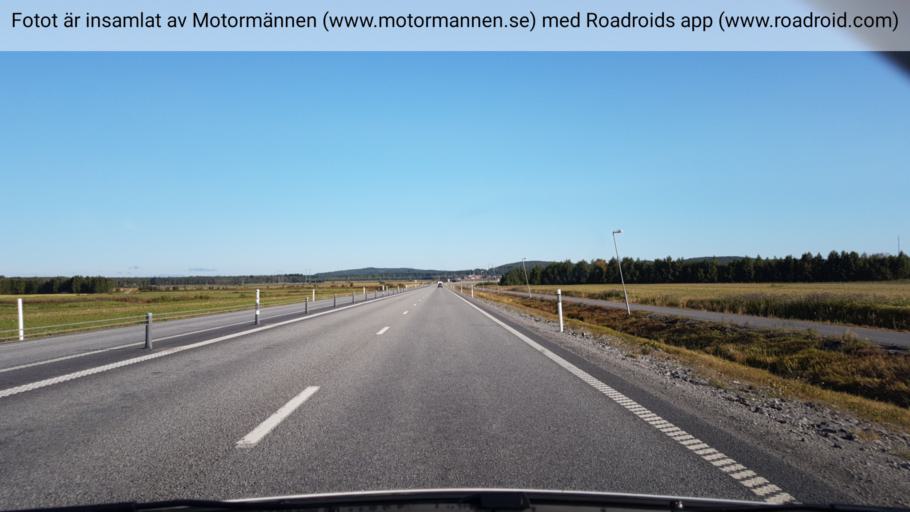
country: SE
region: Vaesterbotten
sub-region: Umea Kommun
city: Roback
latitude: 63.8452
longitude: 20.1910
